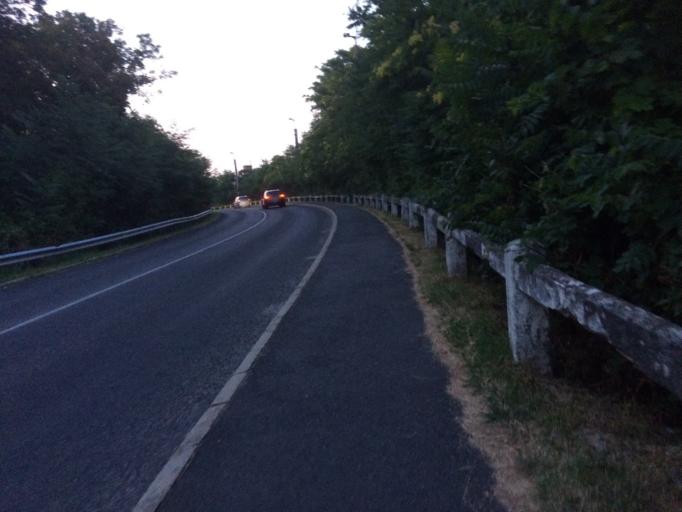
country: HU
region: Veszprem
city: Badacsonytomaj
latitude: 46.8002
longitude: 17.5167
